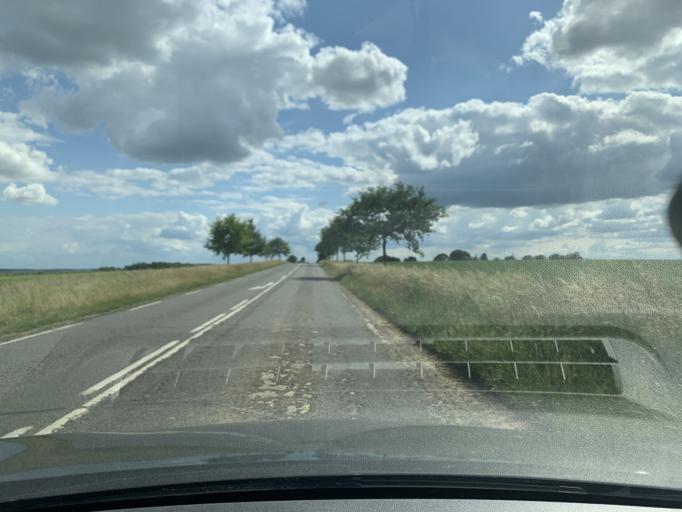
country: FR
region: Picardie
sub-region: Departement de la Somme
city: Moislains
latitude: 49.9692
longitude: 2.9885
